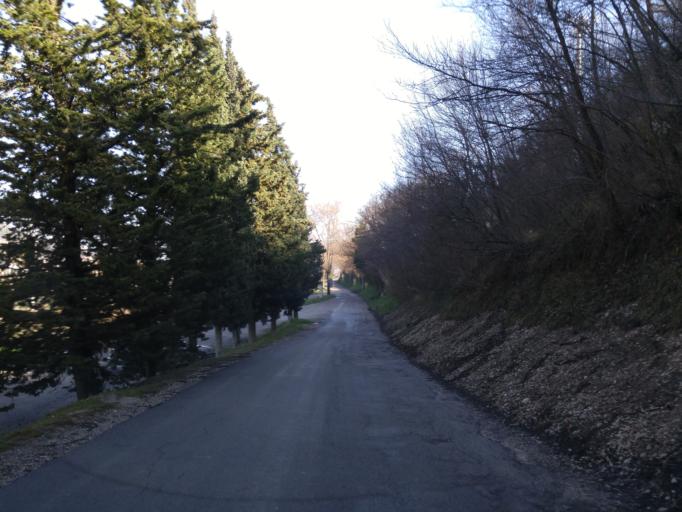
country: IT
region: The Marches
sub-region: Provincia di Pesaro e Urbino
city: Fossombrone
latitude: 43.6800
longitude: 12.8000
